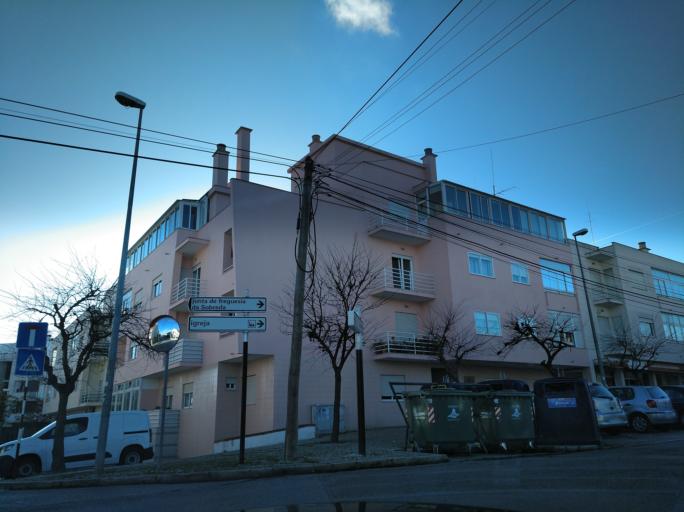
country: PT
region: Setubal
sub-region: Almada
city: Sobreda
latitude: 38.6445
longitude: -9.1850
